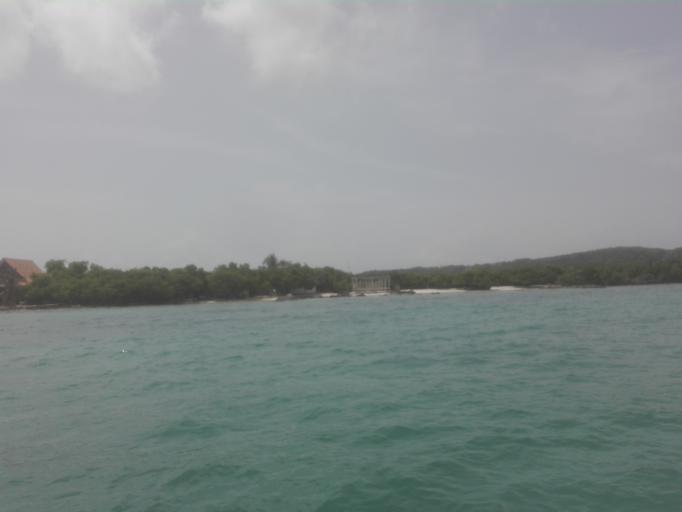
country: CO
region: Bolivar
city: Turbana
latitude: 10.1667
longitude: -75.6701
